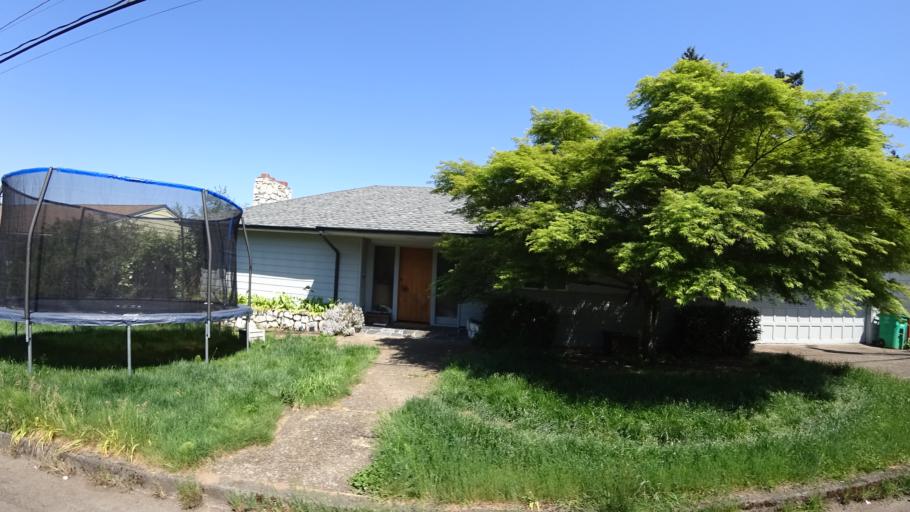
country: US
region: Oregon
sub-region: Clackamas County
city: Milwaukie
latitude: 45.4654
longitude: -122.6804
